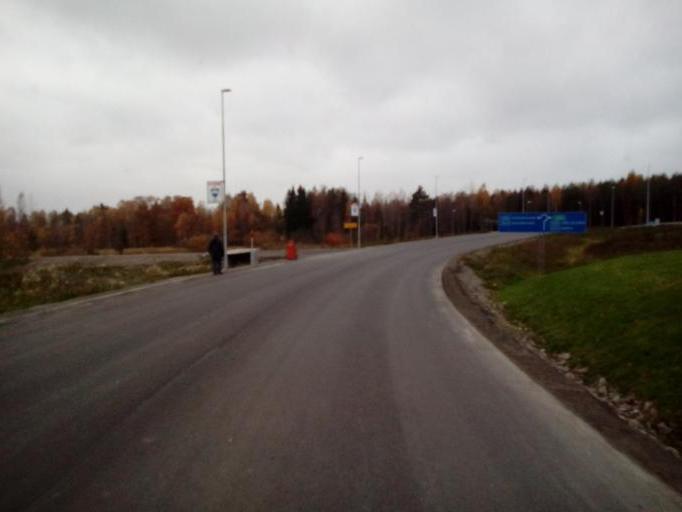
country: SE
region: OErebro
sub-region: Karlskoga Kommun
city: Karlskoga
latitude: 59.2957
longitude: 14.4895
